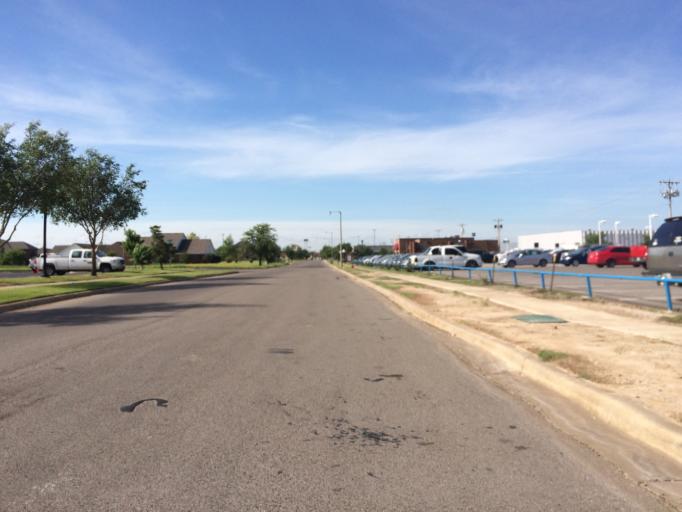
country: US
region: Oklahoma
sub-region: Cleveland County
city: Norman
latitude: 35.2308
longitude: -97.4829
